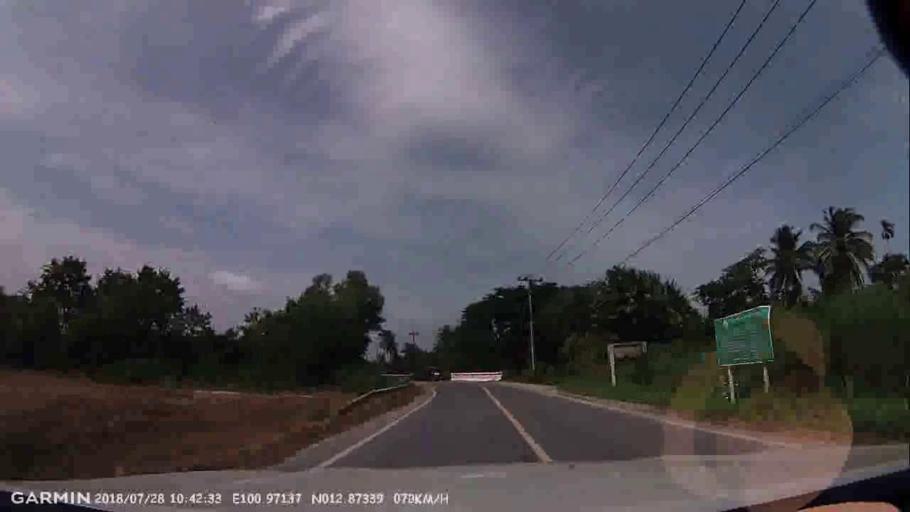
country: TH
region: Chon Buri
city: Phatthaya
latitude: 12.8733
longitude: 100.9713
